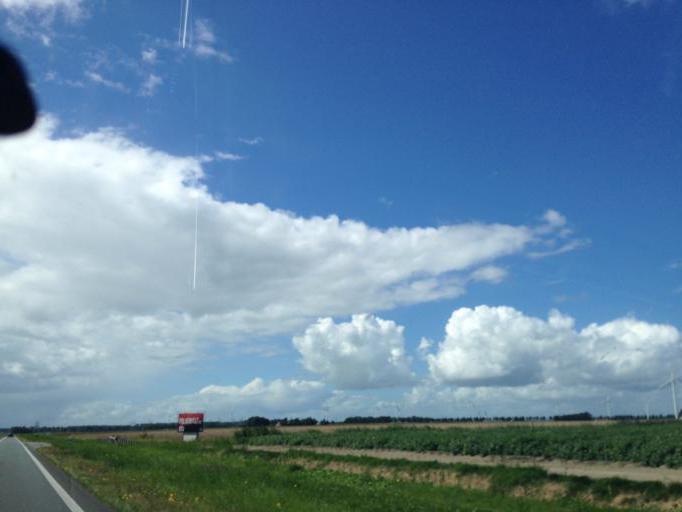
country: NL
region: Flevoland
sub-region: Gemeente Urk
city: Urk
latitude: 52.5492
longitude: 5.5898
